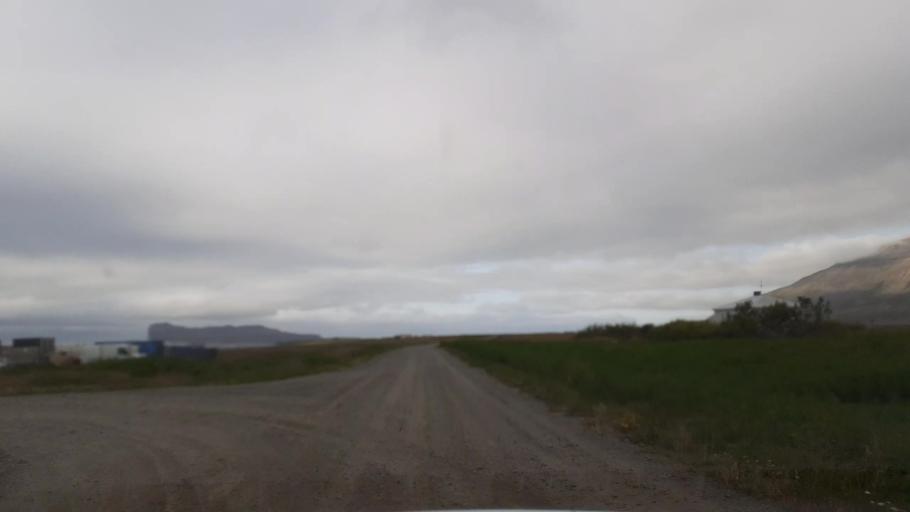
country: IS
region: Northwest
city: Saudarkrokur
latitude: 65.9009
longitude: -19.4221
